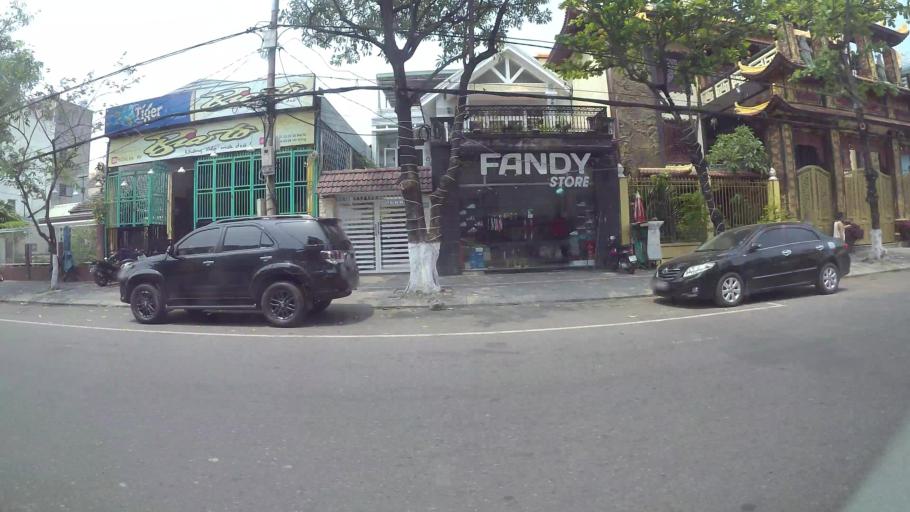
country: VN
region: Da Nang
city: Da Nang
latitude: 16.0778
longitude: 108.2167
